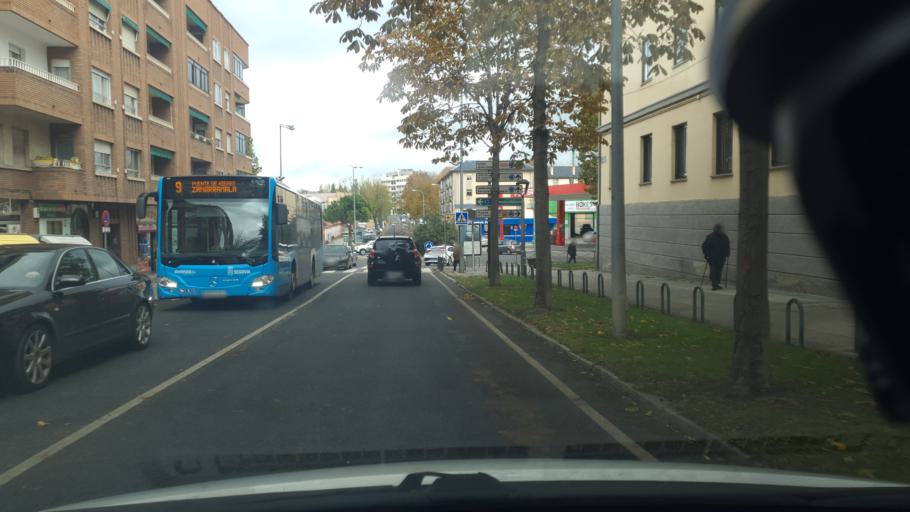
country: ES
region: Castille and Leon
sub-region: Provincia de Segovia
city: Segovia
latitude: 40.9370
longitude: -4.1116
